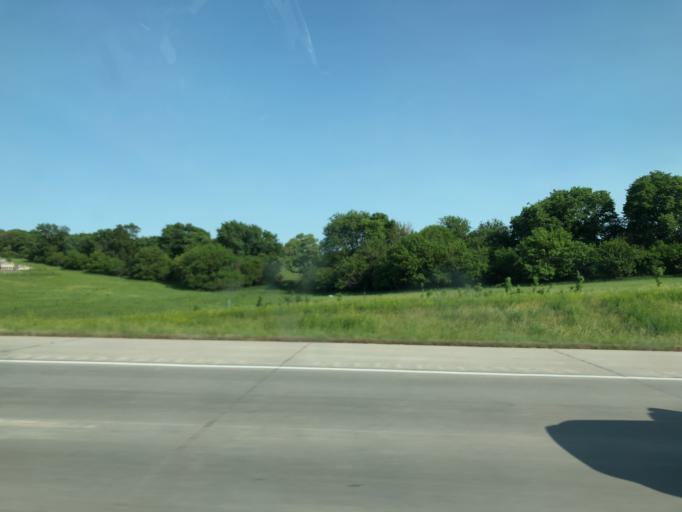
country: US
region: Nebraska
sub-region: Saunders County
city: Ashland
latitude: 40.9651
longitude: -96.3985
